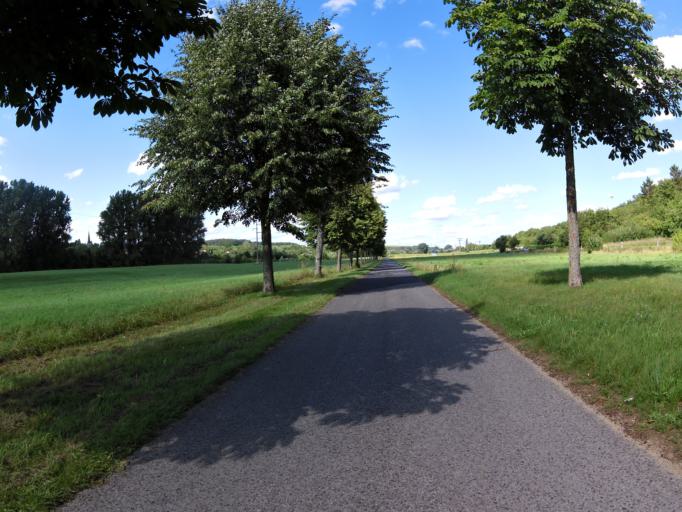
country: DE
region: Bavaria
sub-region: Regierungsbezirk Unterfranken
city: Sulzfeld am Main
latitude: 49.7015
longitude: 10.1343
